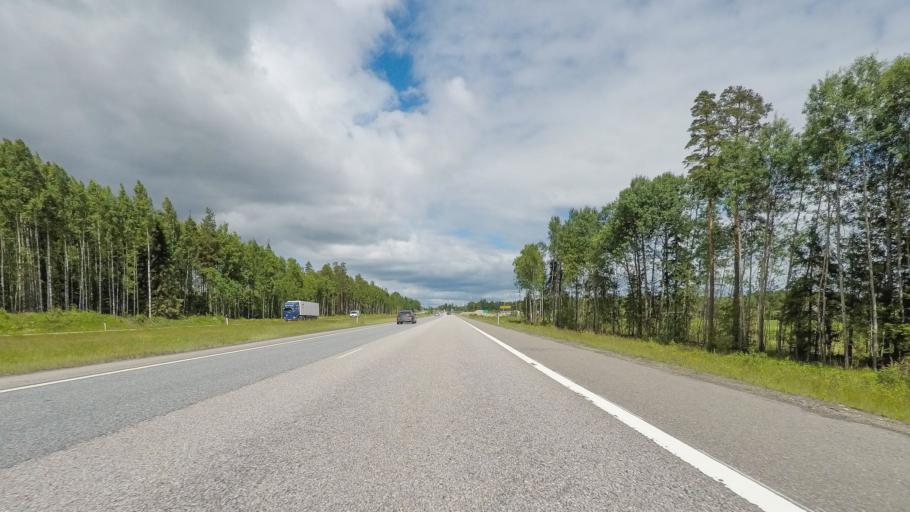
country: FI
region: Uusimaa
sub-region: Helsinki
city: Kerava
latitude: 60.4333
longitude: 25.1259
